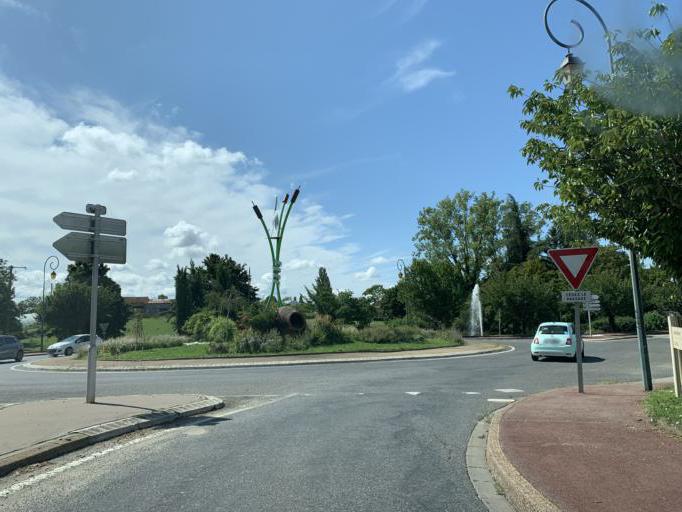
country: FR
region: Rhone-Alpes
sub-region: Departement du Rhone
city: Jons
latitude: 45.8015
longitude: 5.0870
